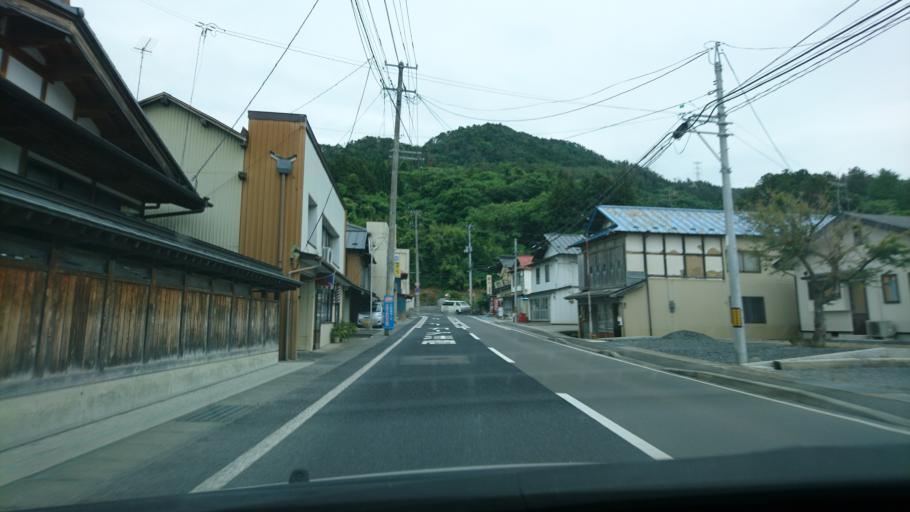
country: JP
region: Iwate
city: Ichinoseki
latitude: 38.9558
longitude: 141.2568
